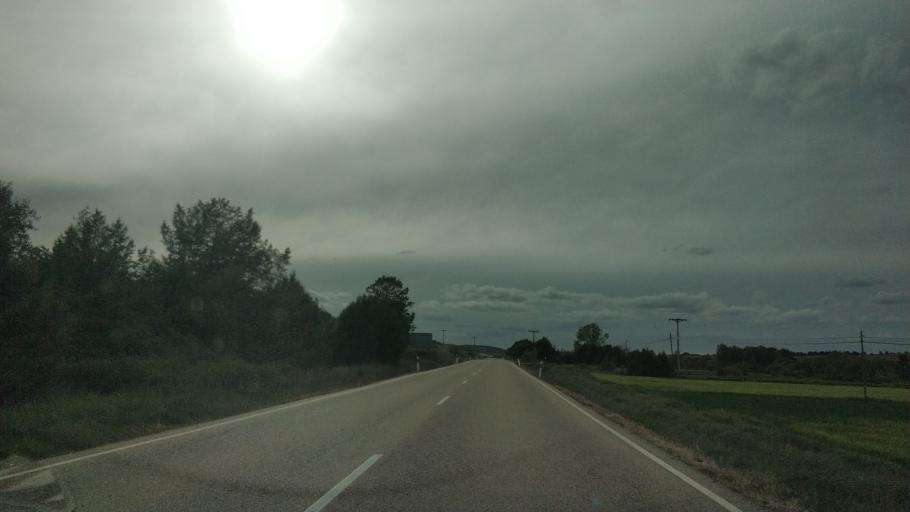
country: ES
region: Castille and Leon
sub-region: Provincia de Soria
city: Valdenebro
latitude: 41.5660
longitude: -2.9982
